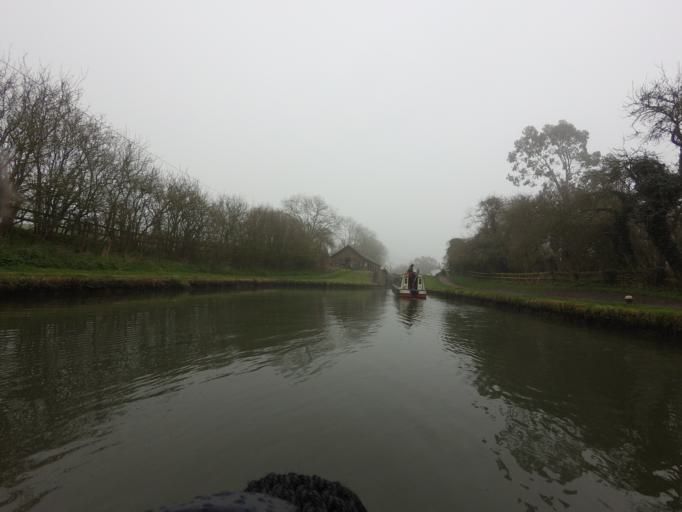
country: GB
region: England
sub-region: Hertfordshire
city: Tring
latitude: 51.8161
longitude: -0.6550
